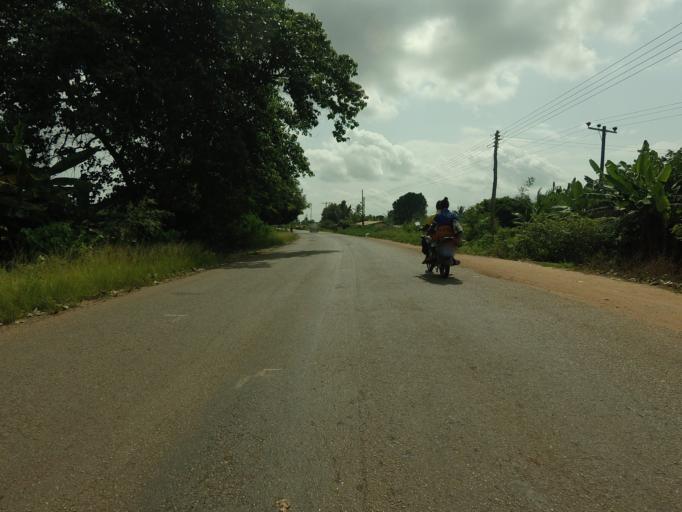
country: TG
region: Maritime
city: Lome
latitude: 6.2207
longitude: 1.0430
